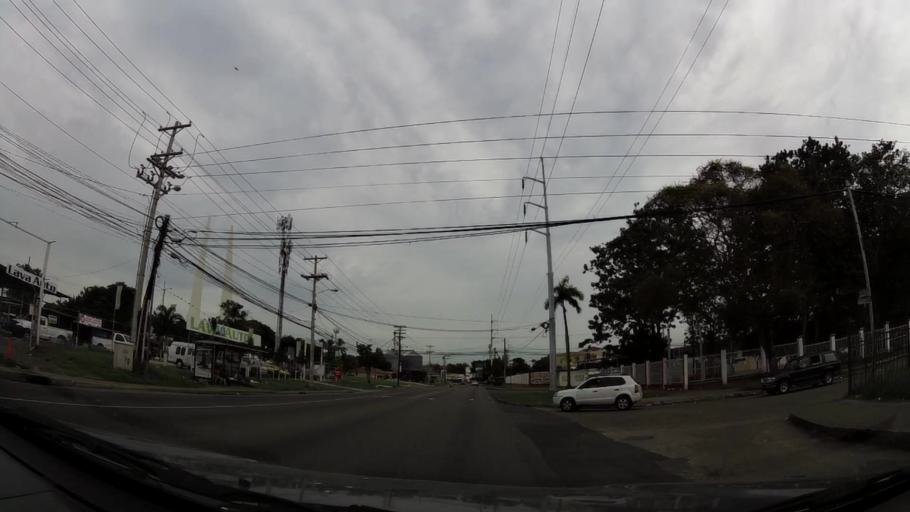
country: PA
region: Panama
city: San Miguelito
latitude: 9.0343
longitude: -79.4731
